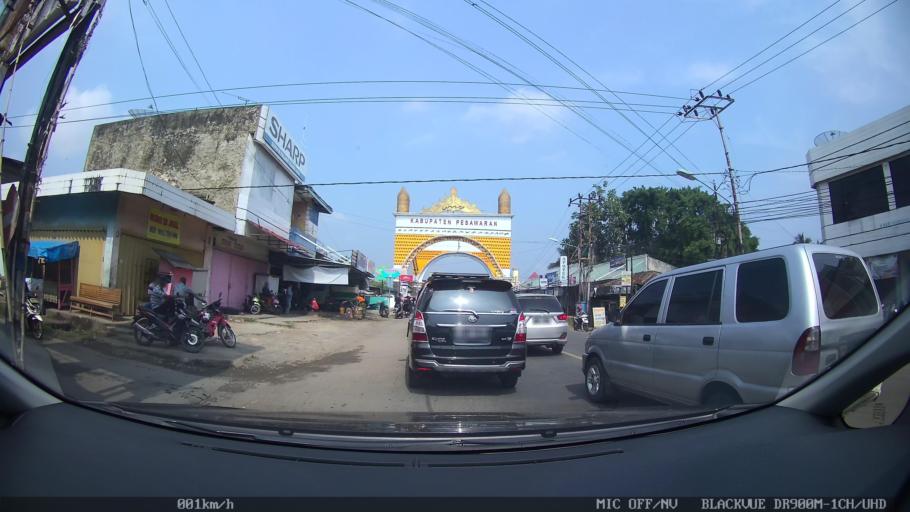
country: ID
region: Lampung
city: Gedongtataan
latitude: -5.3800
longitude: 105.0971
